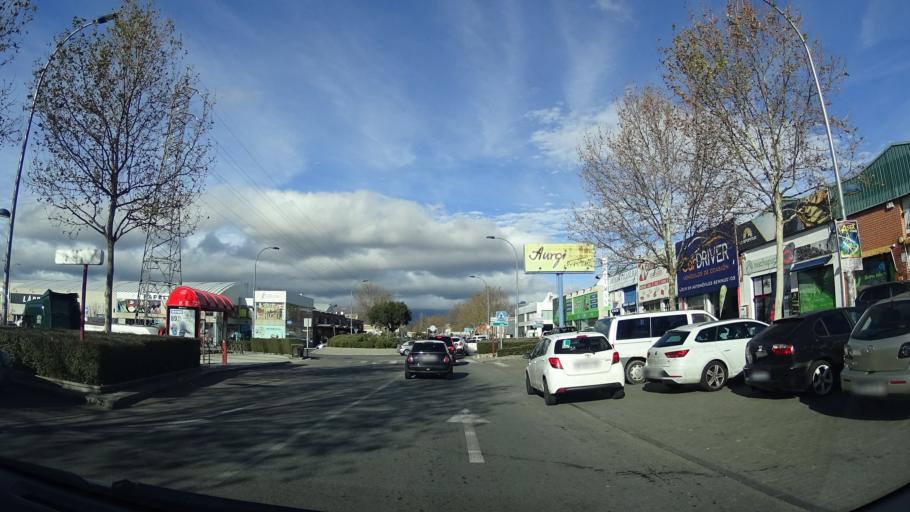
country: ES
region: Madrid
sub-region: Provincia de Madrid
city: Collado-Villalba
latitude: 40.6260
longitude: -4.0172
